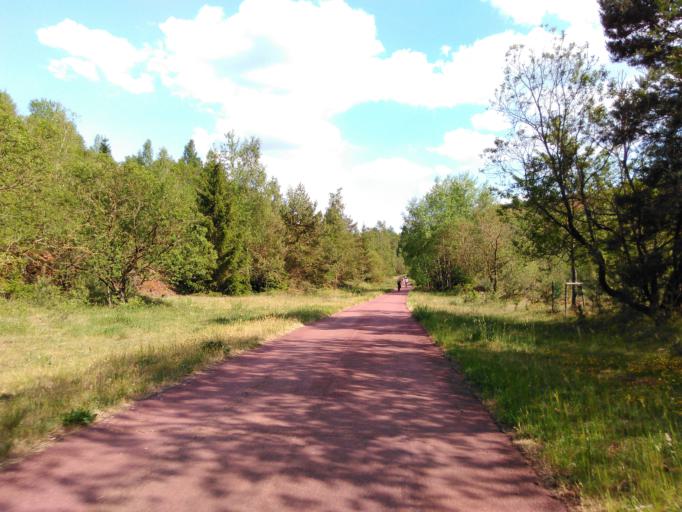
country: LU
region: Luxembourg
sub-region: Canton d'Esch-sur-Alzette
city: Rumelange
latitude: 49.4720
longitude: 6.0185
